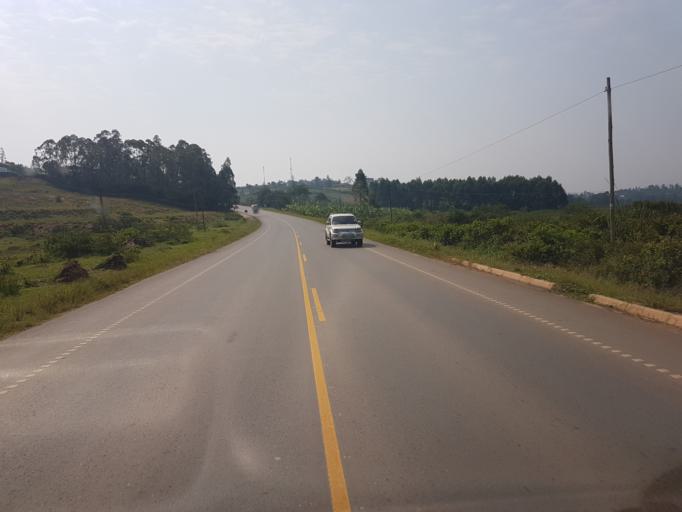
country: UG
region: Western Region
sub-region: Mbarara District
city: Bwizibwera
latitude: -0.6426
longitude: 30.5838
